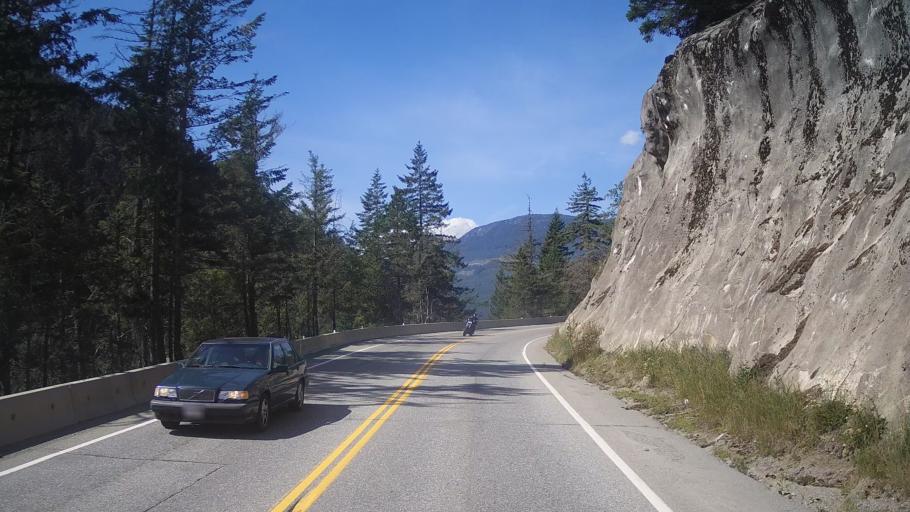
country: CA
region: British Columbia
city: Pemberton
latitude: 50.2882
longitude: -122.8385
